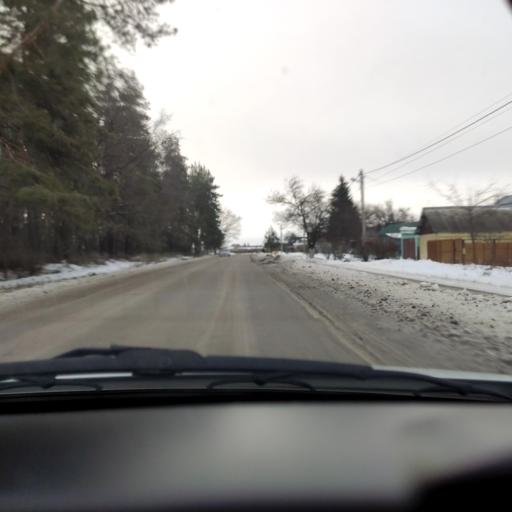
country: RU
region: Voronezj
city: Ramon'
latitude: 51.8985
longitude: 39.2859
